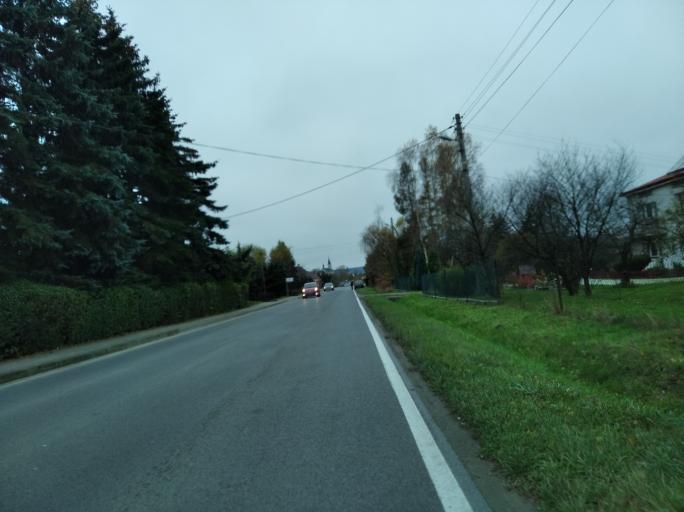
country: PL
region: Subcarpathian Voivodeship
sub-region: Powiat krosnienski
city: Chorkowka
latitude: 49.6732
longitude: 21.6983
